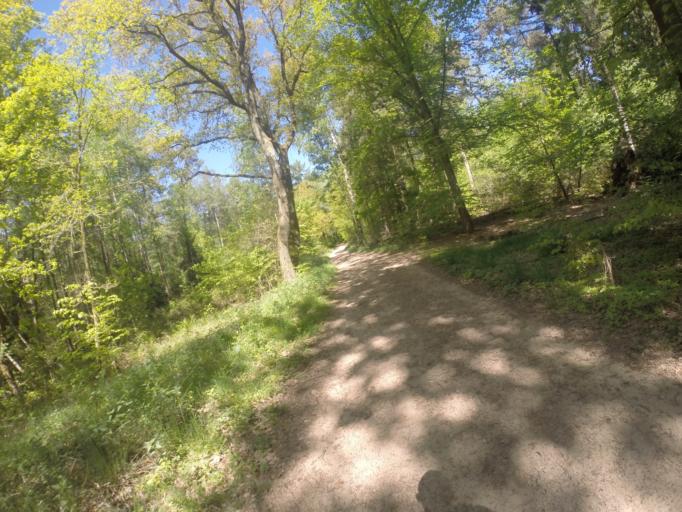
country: NL
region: Gelderland
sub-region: Gemeente Montferland
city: s-Heerenberg
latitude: 51.9066
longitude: 6.2398
